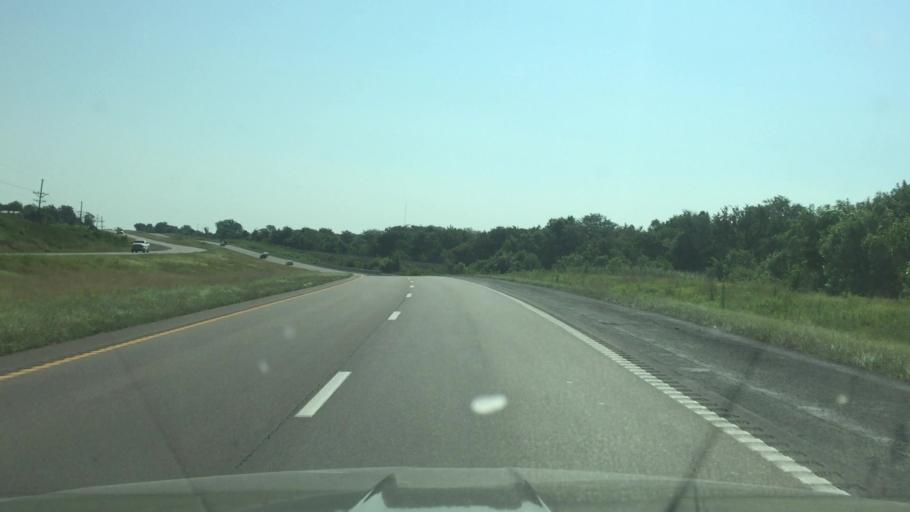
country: US
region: Missouri
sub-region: Johnson County
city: Knob Noster
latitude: 38.7720
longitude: -93.6444
